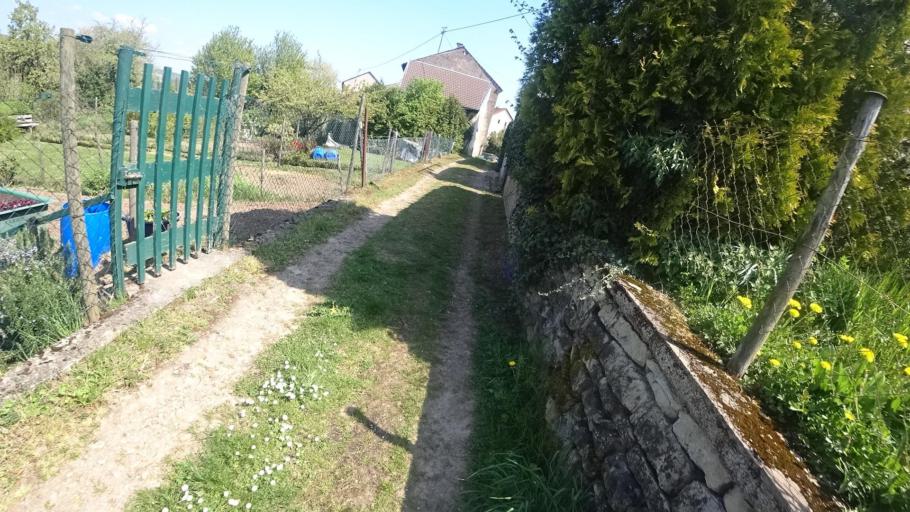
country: DE
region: Rheinland-Pfalz
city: Temmels
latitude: 49.6879
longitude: 6.4639
